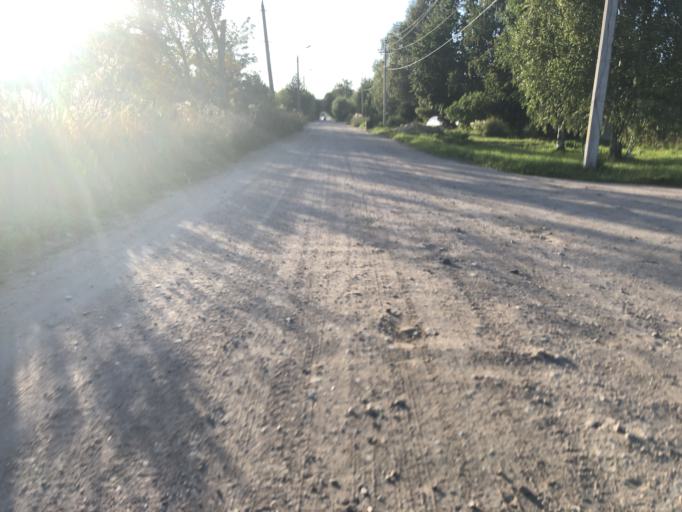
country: RU
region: Tverskaya
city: Rzhev
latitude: 56.2441
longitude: 34.3060
